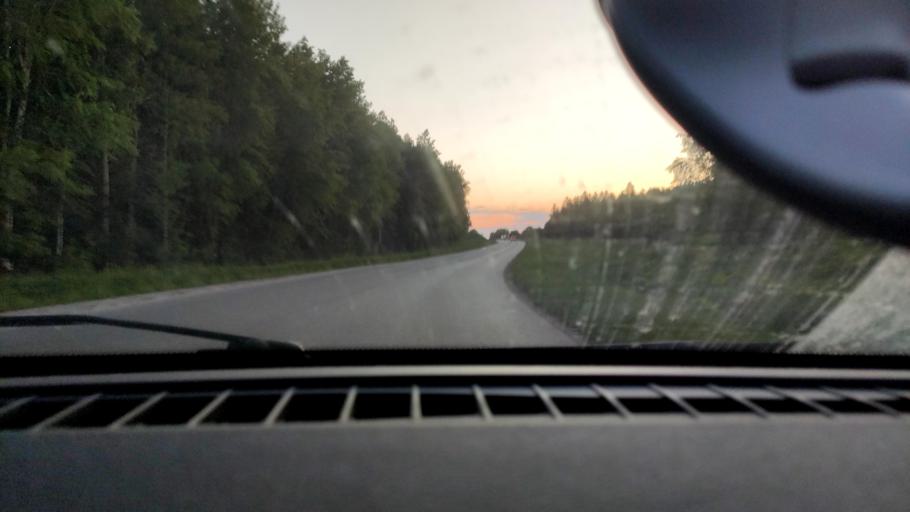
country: RU
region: Perm
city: Polazna
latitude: 58.2102
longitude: 56.4488
